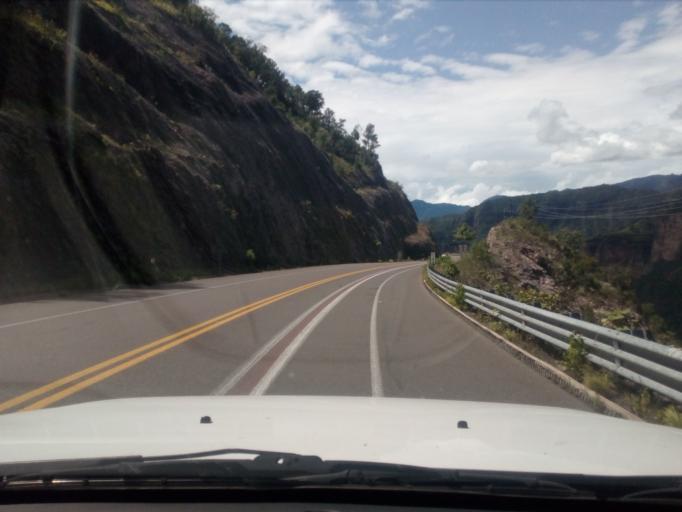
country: MX
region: Durango
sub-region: Pueblo Nuevo
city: La Ciudad
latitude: 23.6217
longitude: -105.6870
